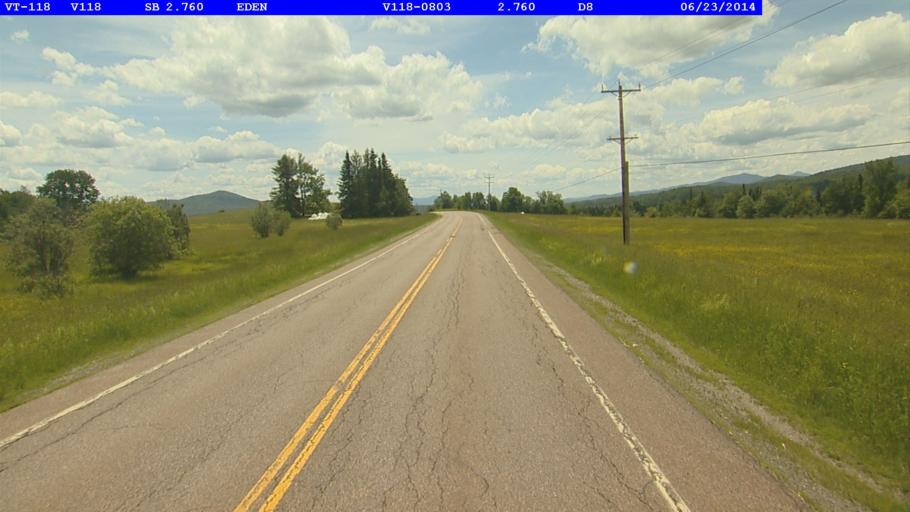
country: US
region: Vermont
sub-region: Lamoille County
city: Johnson
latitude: 44.7426
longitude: -72.5664
